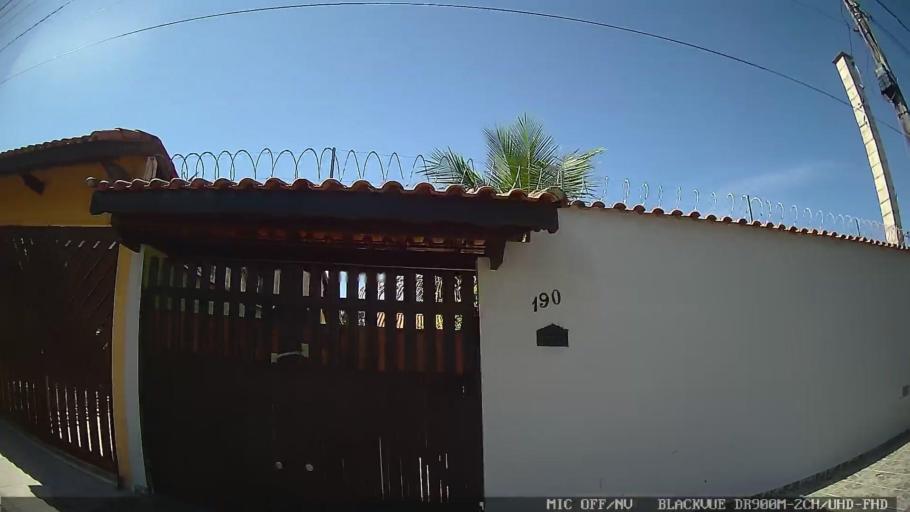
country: BR
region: Sao Paulo
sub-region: Peruibe
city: Peruibe
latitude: -24.2775
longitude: -46.9416
